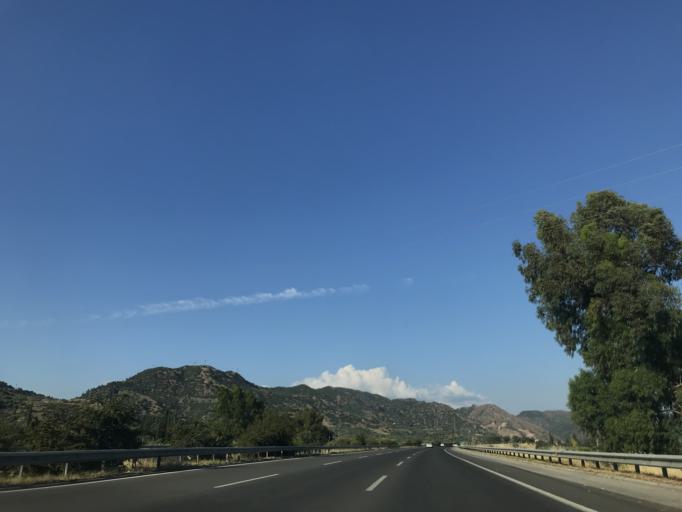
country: TR
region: Aydin
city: Incirliova
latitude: 37.8745
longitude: 27.6758
